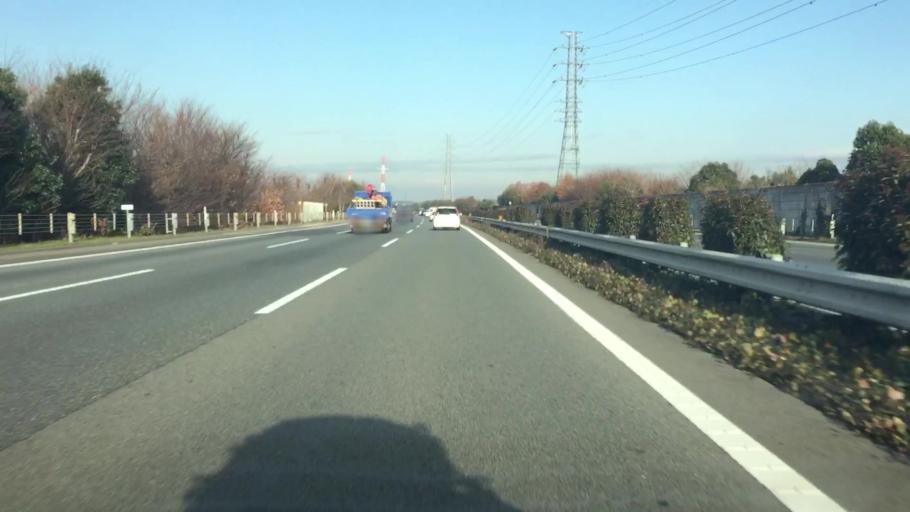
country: JP
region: Saitama
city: Yorii
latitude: 36.1532
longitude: 139.2180
